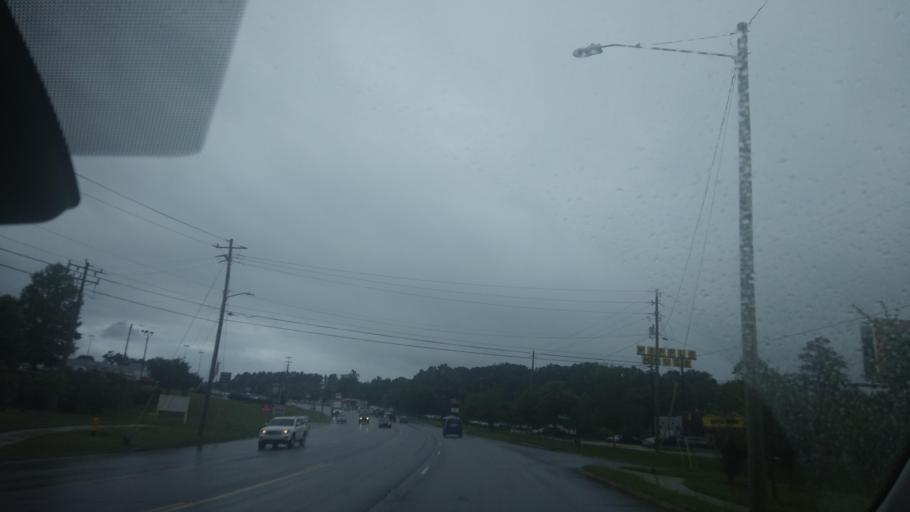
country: US
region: North Carolina
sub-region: Buncombe County
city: Bent Creek
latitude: 35.5609
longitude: -82.6334
